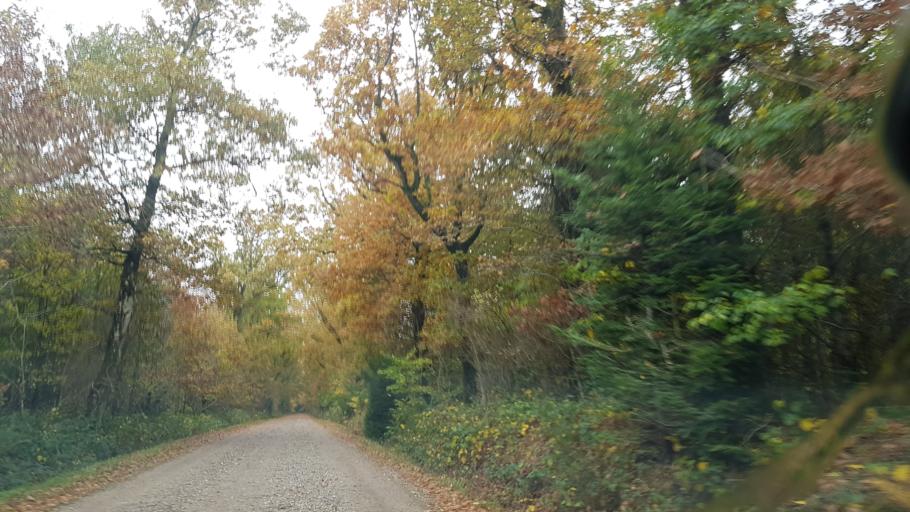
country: DK
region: South Denmark
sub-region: Tonder Kommune
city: Sherrebek
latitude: 55.1783
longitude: 8.7654
